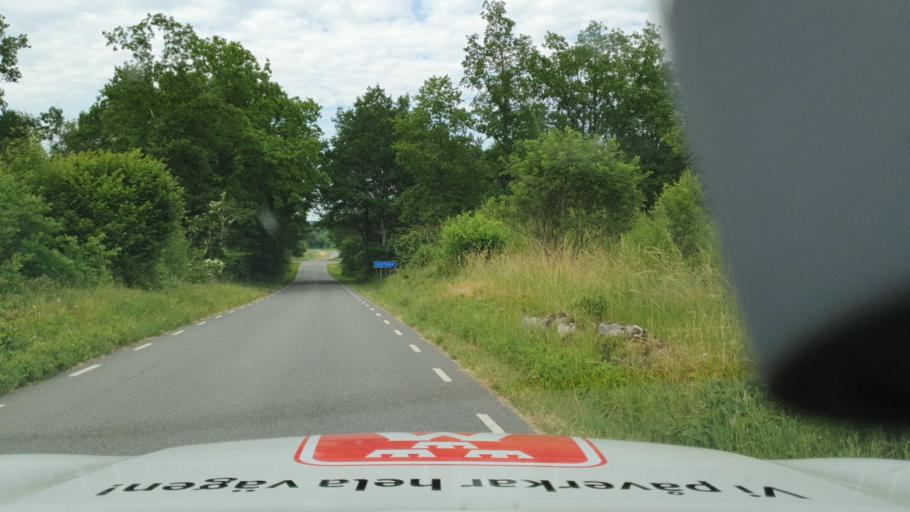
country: SE
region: Skane
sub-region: Kristianstads Kommun
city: Degeberga
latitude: 55.7351
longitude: 13.9338
